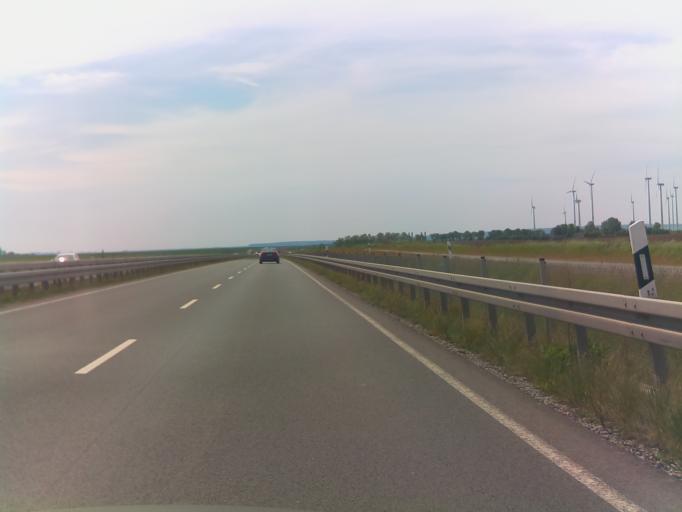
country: DE
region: Saxony-Anhalt
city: Wolmirsleben
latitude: 51.9944
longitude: 11.4890
